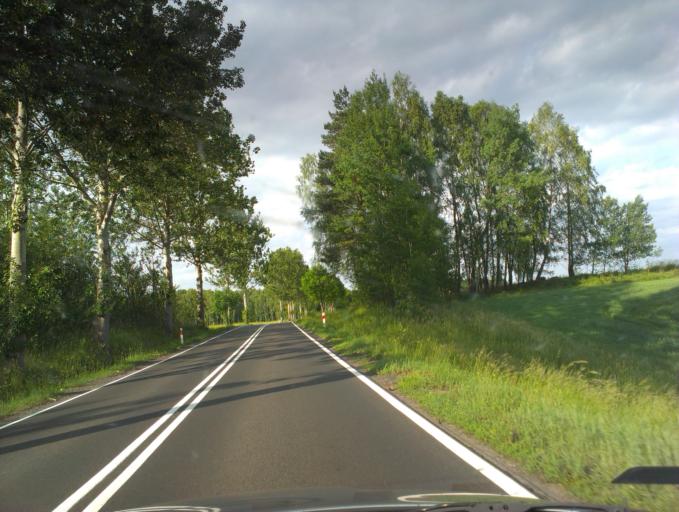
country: PL
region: West Pomeranian Voivodeship
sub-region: Powiat szczecinecki
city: Borne Sulinowo
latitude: 53.6167
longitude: 16.5901
